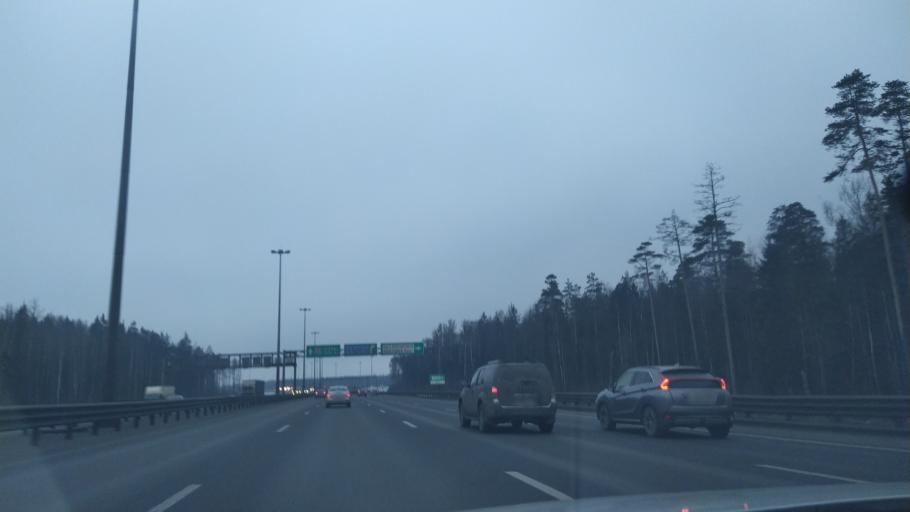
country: RU
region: Leningrad
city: Yanino Vtoroye
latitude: 59.9528
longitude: 30.5467
